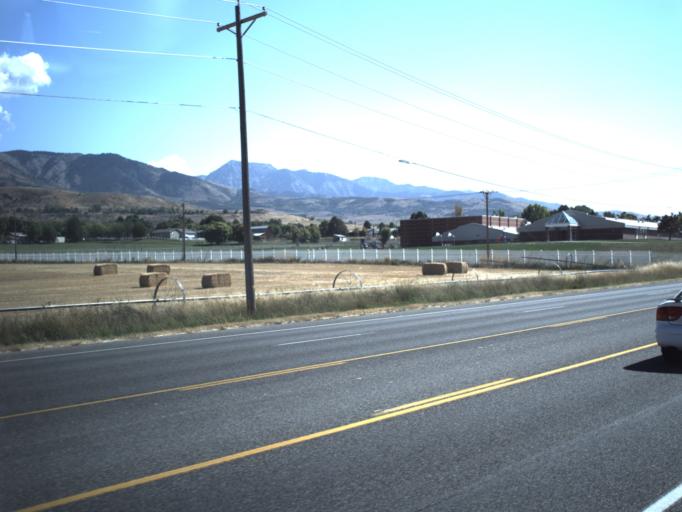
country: US
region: Utah
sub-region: Cache County
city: Richmond
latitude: 41.9288
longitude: -111.8143
